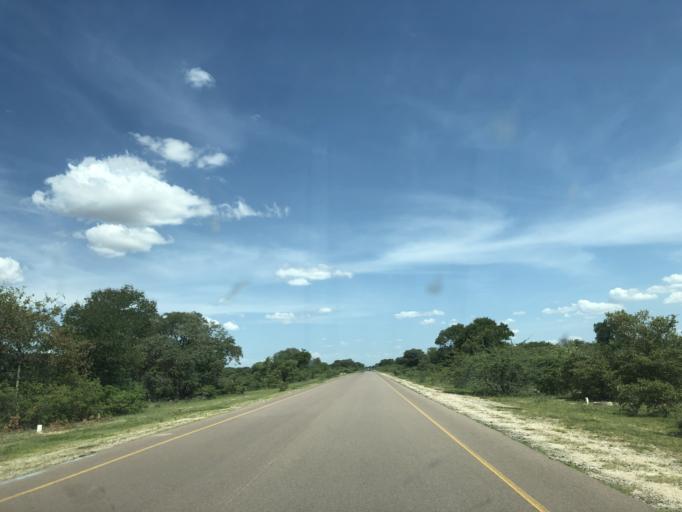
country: AO
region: Cunene
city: Ondjiva
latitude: -16.8640
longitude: 15.4759
